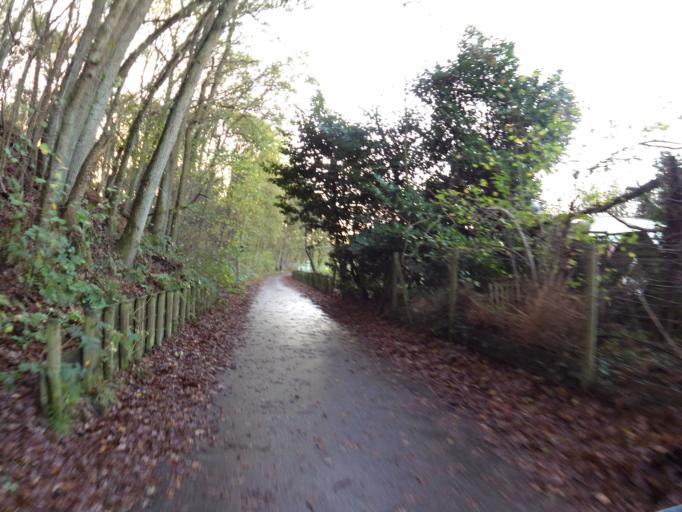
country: NL
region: North Brabant
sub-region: Gemeente Waalwijk
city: Waalwijk
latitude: 51.6573
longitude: 5.0892
